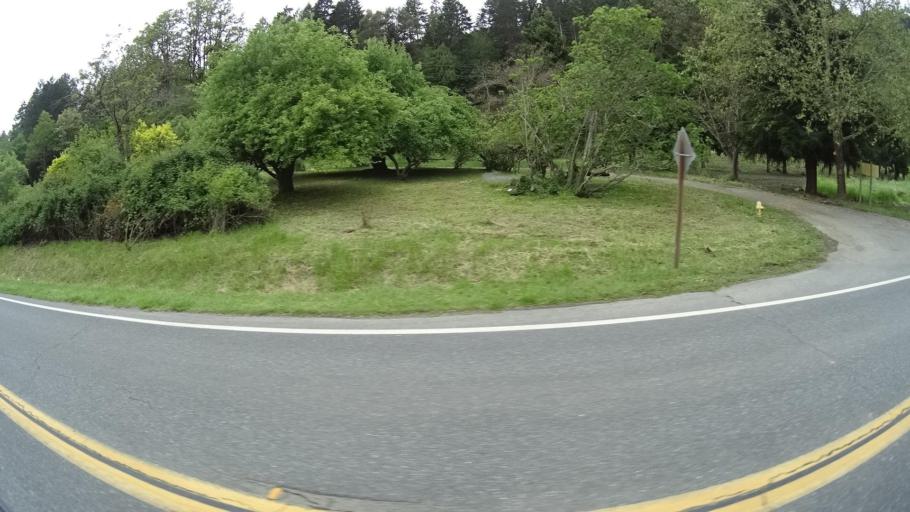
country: US
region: California
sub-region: Humboldt County
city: Willow Creek
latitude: 40.9744
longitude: -123.6399
